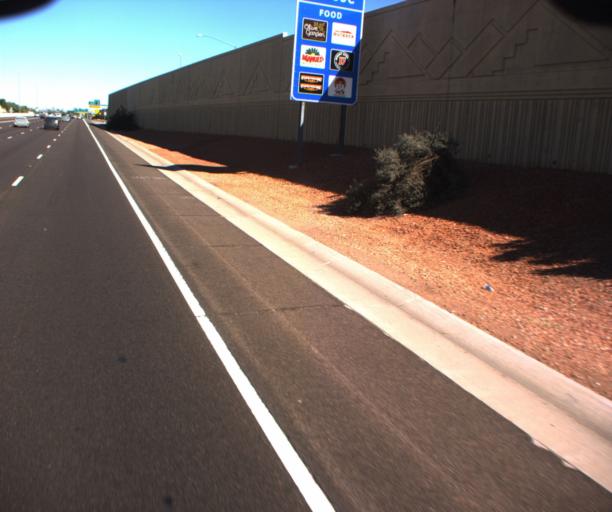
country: US
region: Arizona
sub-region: Maricopa County
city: San Carlos
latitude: 33.3660
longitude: -111.8936
